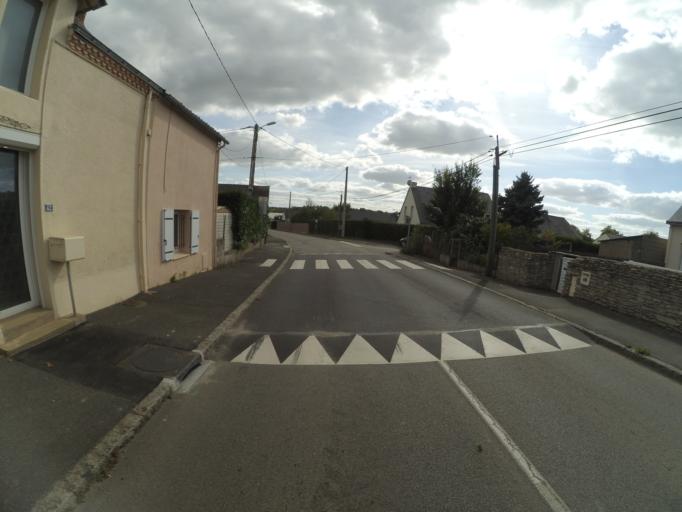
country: FR
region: Pays de la Loire
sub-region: Departement de la Loire-Atlantique
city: Carquefou
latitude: 47.3098
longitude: -1.5075
